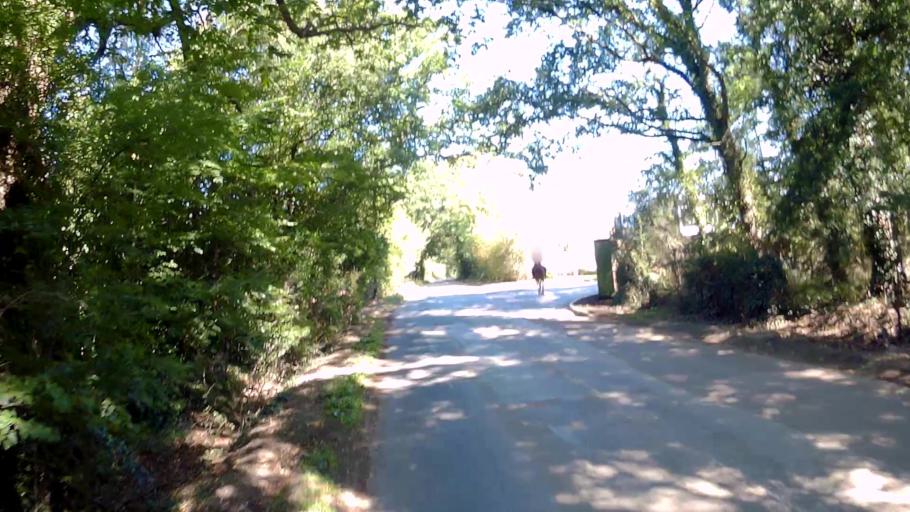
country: GB
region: England
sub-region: Hampshire
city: Eversley
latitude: 51.3744
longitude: -0.9028
